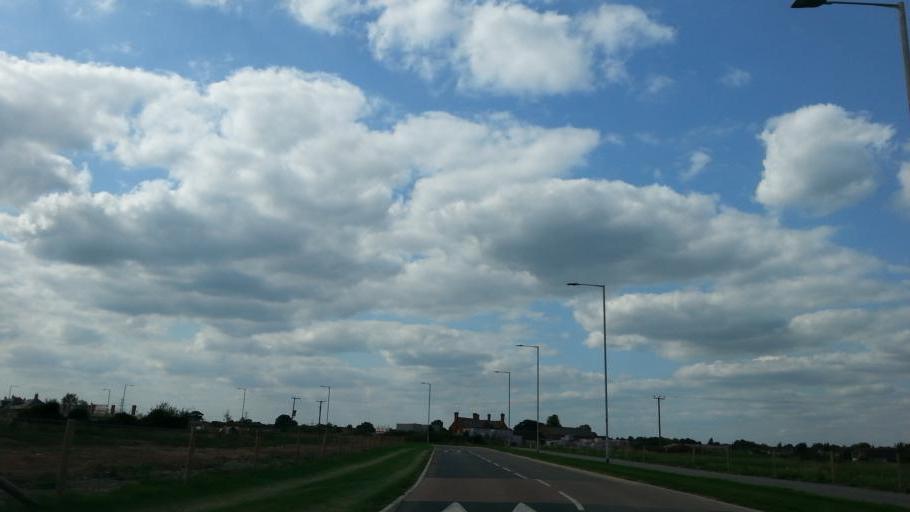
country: GB
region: England
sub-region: Leicestershire
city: Kirby Muxloe
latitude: 52.6149
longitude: -1.2143
